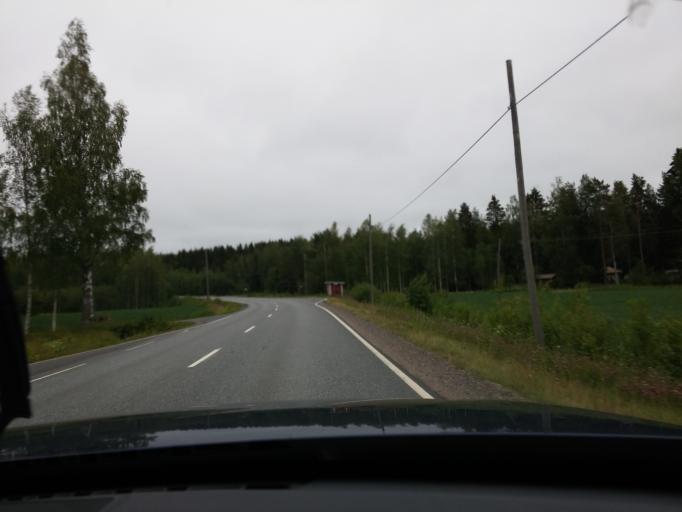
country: FI
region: Central Finland
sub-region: Joutsa
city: Joutsa
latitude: 61.7839
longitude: 26.0565
